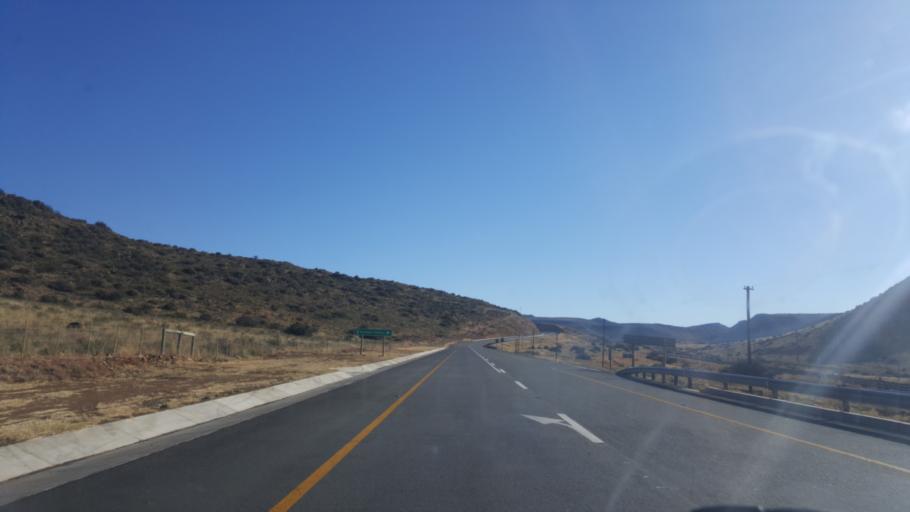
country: ZA
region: Eastern Cape
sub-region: Chris Hani District Municipality
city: Middelburg
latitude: -31.3857
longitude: 25.0316
